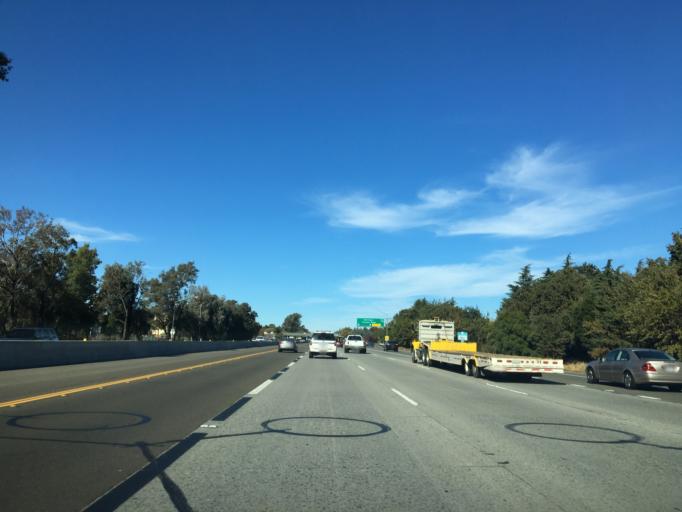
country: US
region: California
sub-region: Contra Costa County
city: San Ramon
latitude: 37.7550
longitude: -121.9620
